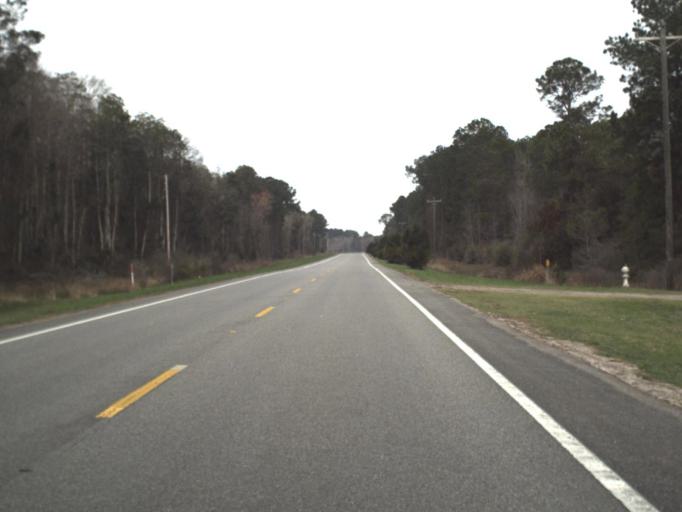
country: US
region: Florida
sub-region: Jefferson County
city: Monticello
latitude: 30.5048
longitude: -83.7645
